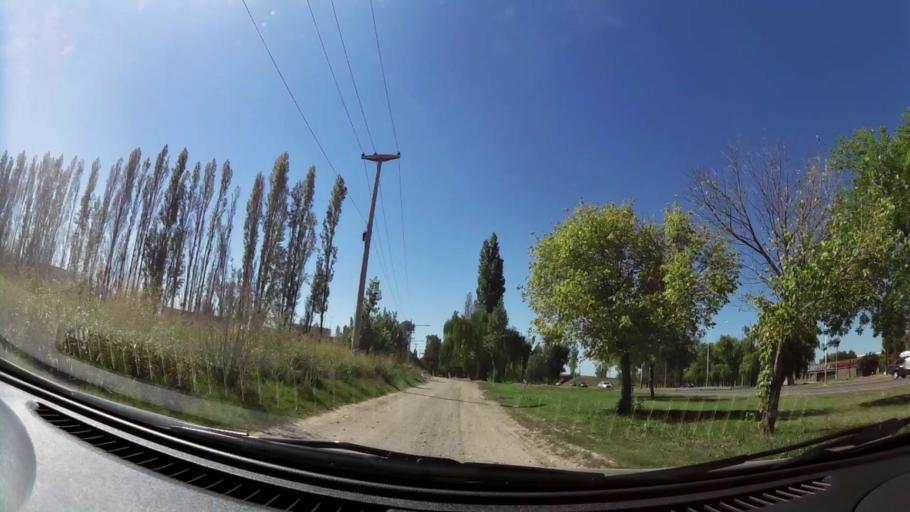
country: AR
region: Mendoza
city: Lujan de Cuyo
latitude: -32.9868
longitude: -68.8510
